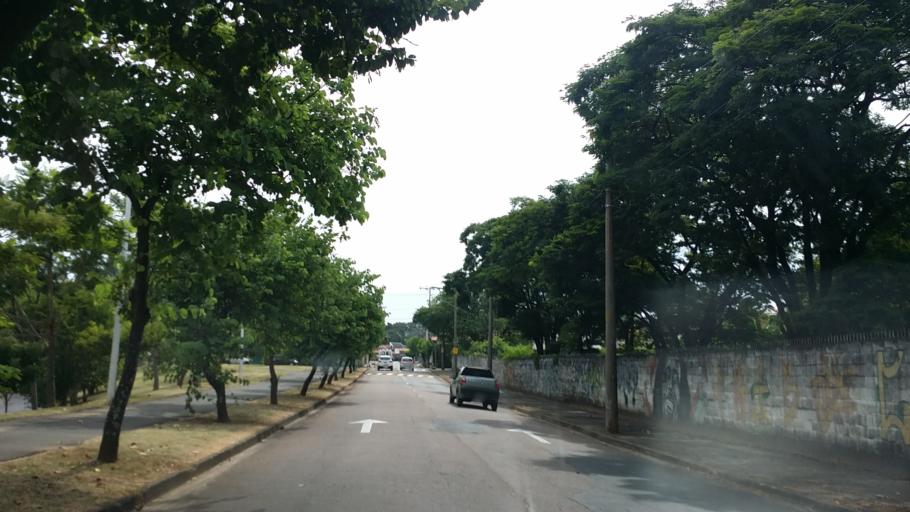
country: BR
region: Sao Paulo
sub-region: Indaiatuba
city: Indaiatuba
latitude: -23.0955
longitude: -47.2188
